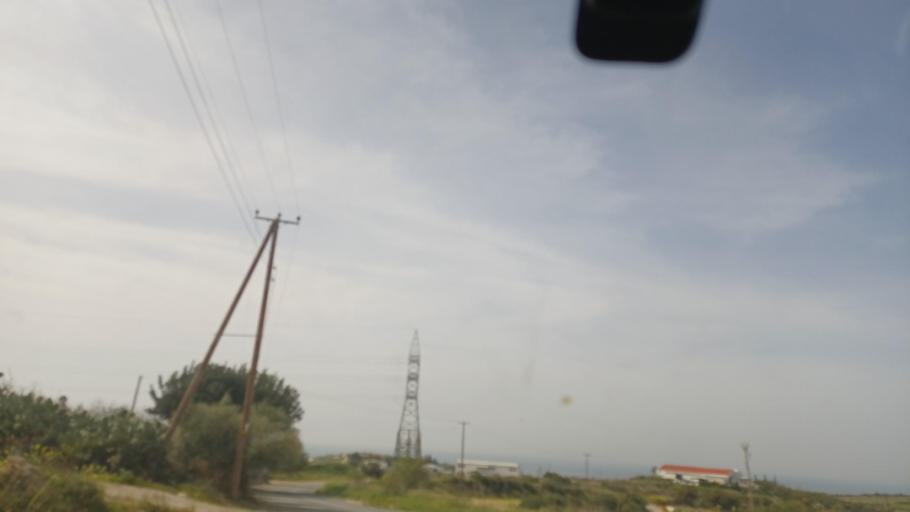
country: CY
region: Pafos
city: Mesogi
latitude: 34.7716
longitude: 32.4805
